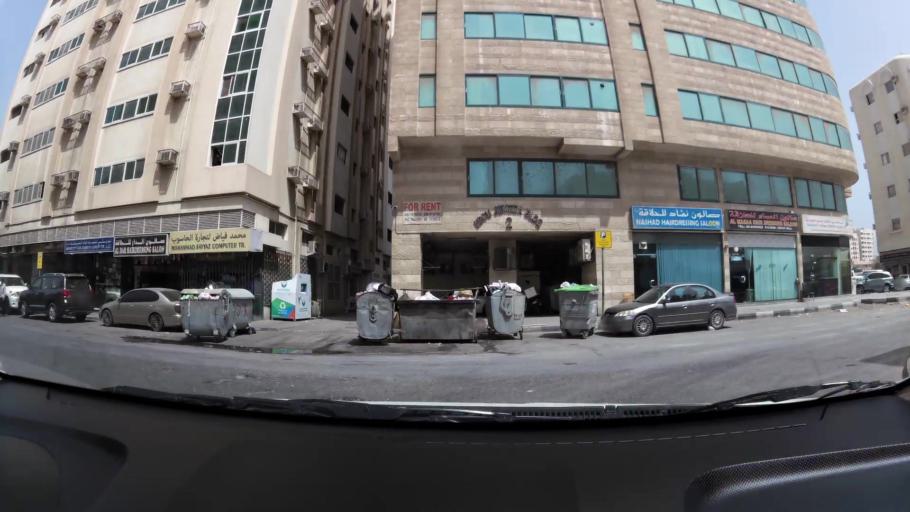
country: AE
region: Ash Shariqah
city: Sharjah
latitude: 25.3551
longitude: 55.3827
